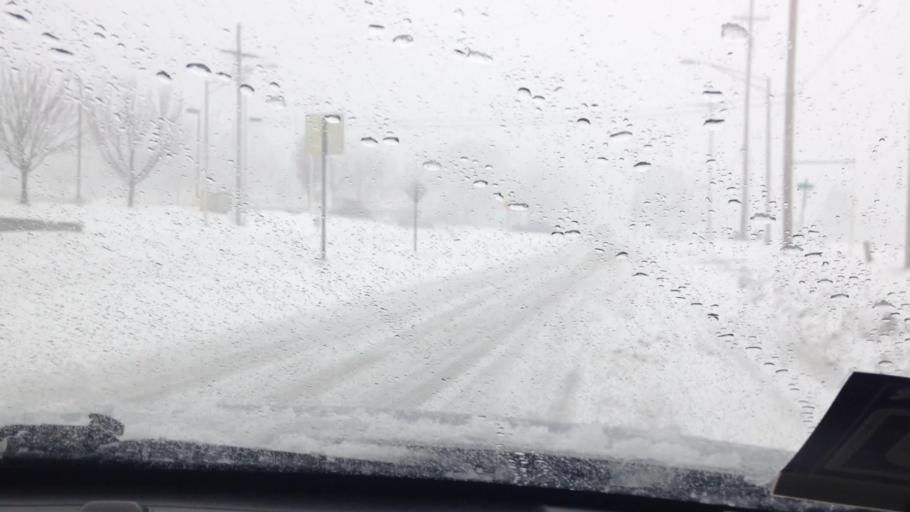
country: US
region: Kansas
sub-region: Johnson County
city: Shawnee
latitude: 39.0150
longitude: -94.7237
